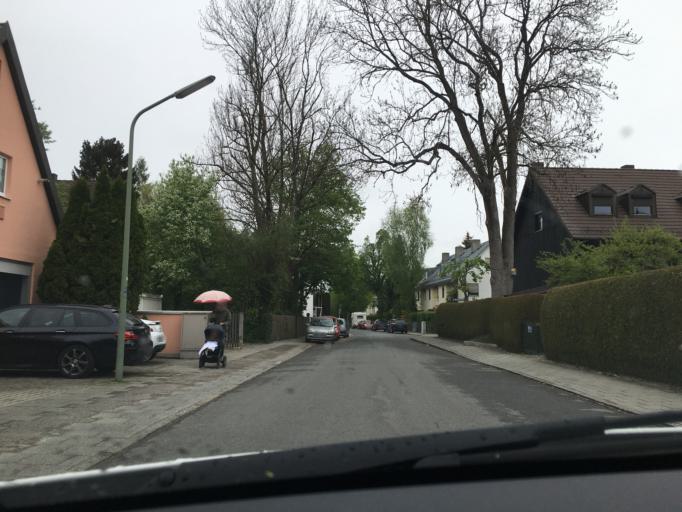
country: DE
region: Bavaria
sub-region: Upper Bavaria
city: Pullach im Isartal
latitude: 48.0778
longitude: 11.5164
